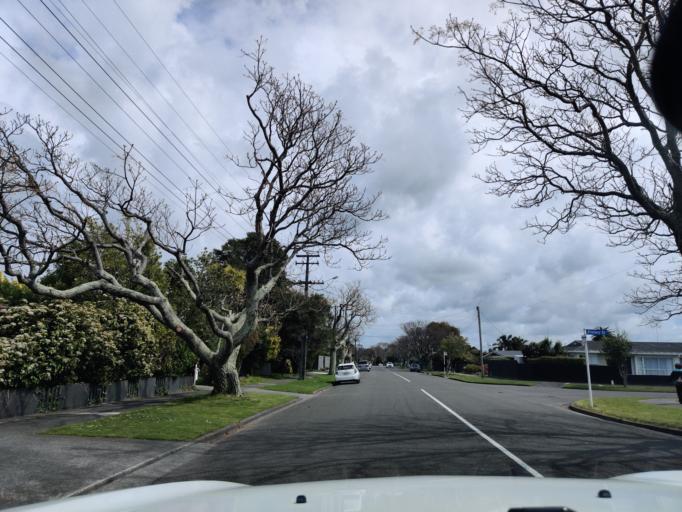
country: NZ
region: Manawatu-Wanganui
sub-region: Palmerston North City
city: Palmerston North
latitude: -40.3799
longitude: 175.5907
